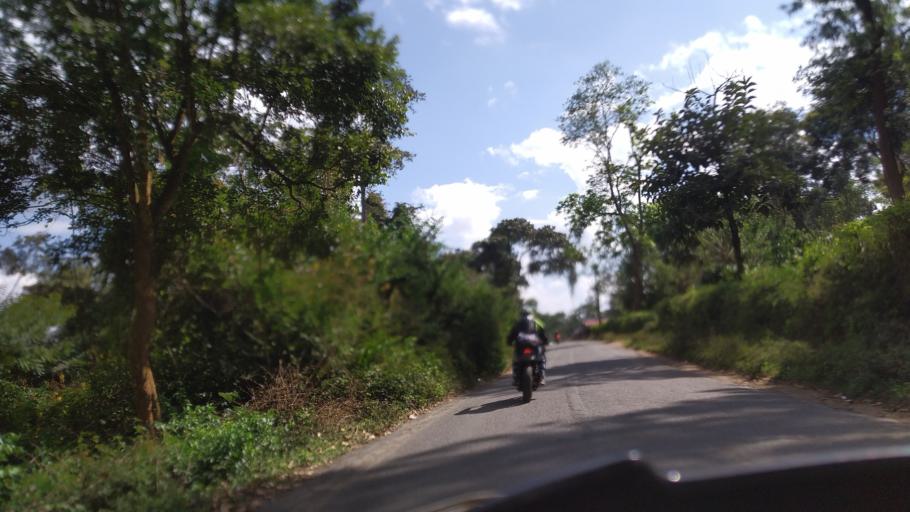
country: IN
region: Karnataka
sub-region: Kodagu
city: Ponnampet
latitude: 11.9591
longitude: 76.0624
